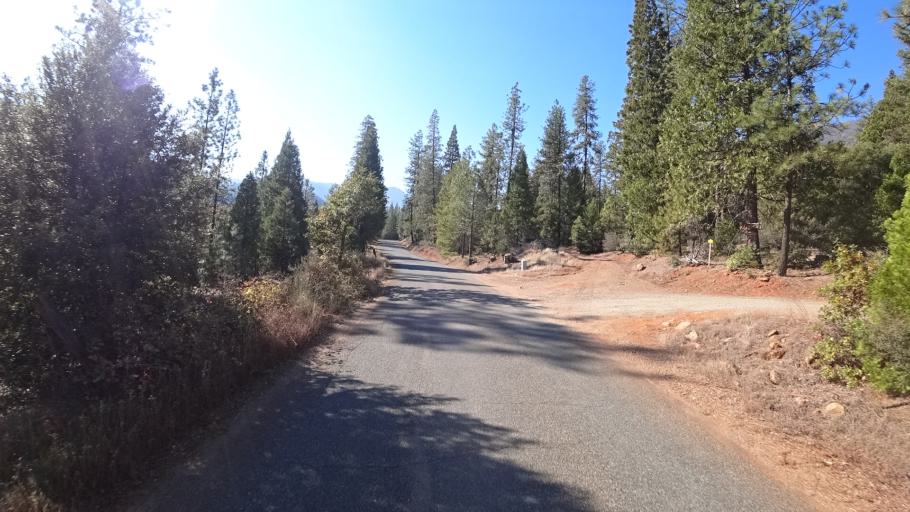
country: US
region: California
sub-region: Siskiyou County
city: Yreka
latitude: 41.7356
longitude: -123.0060
